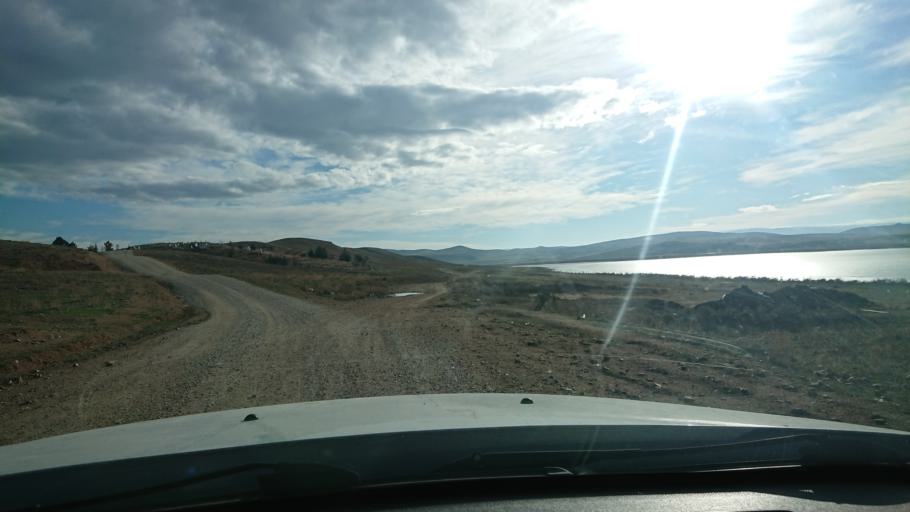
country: TR
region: Aksaray
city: Sariyahsi
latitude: 39.0515
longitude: 33.9748
